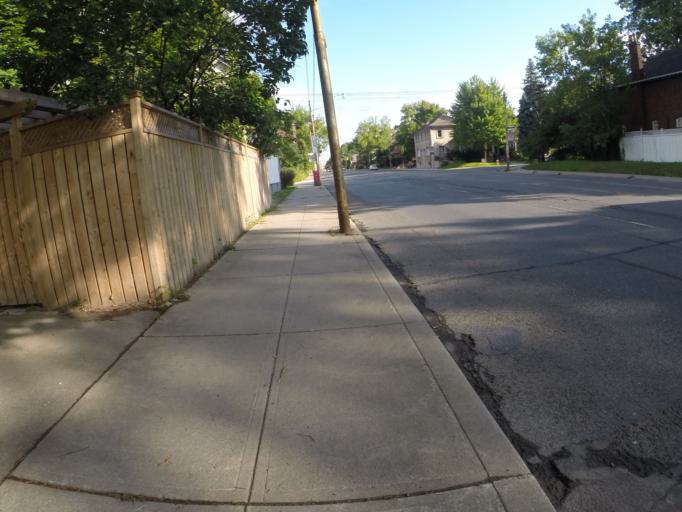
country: CA
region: Ontario
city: Toronto
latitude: 43.6914
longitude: -79.3838
